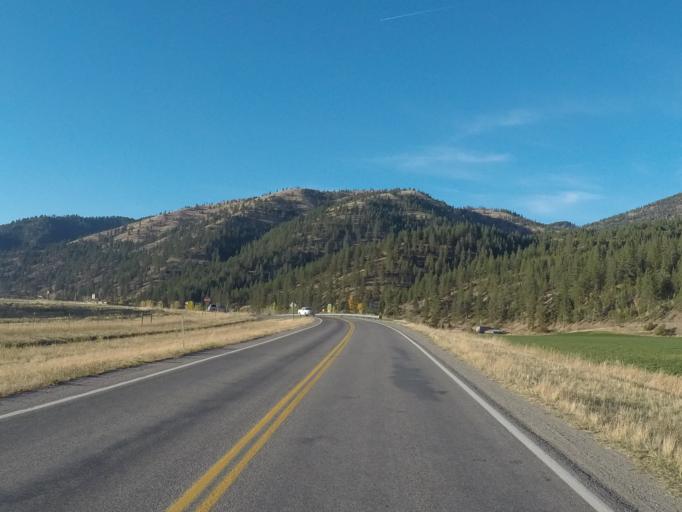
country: US
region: Montana
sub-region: Missoula County
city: Clinton
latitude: 46.7800
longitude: -113.7116
